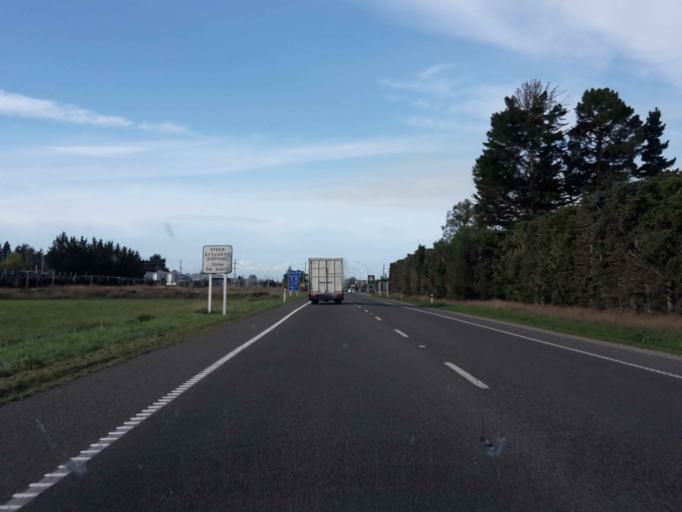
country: NZ
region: Canterbury
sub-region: Ashburton District
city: Tinwald
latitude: -43.9270
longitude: 171.7072
